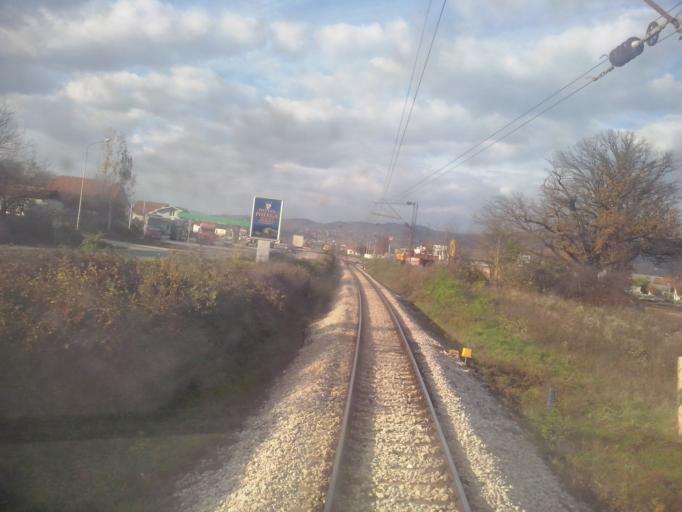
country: RS
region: Central Serbia
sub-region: Zlatiborski Okrug
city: Pozega
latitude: 43.8126
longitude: 20.0357
